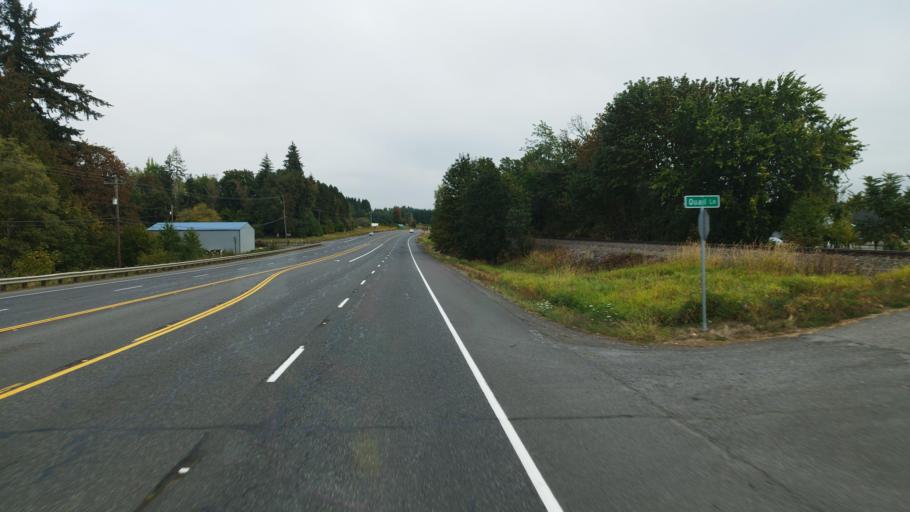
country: US
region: Oregon
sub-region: Columbia County
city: Warren
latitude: 45.7963
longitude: -122.8665
